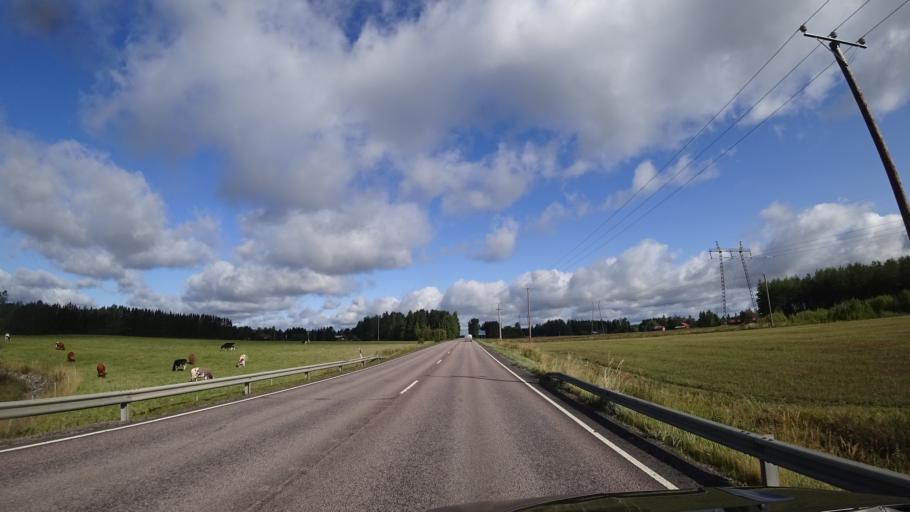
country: FI
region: Uusimaa
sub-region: Helsinki
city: Hyvinge
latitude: 60.5207
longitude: 24.9256
